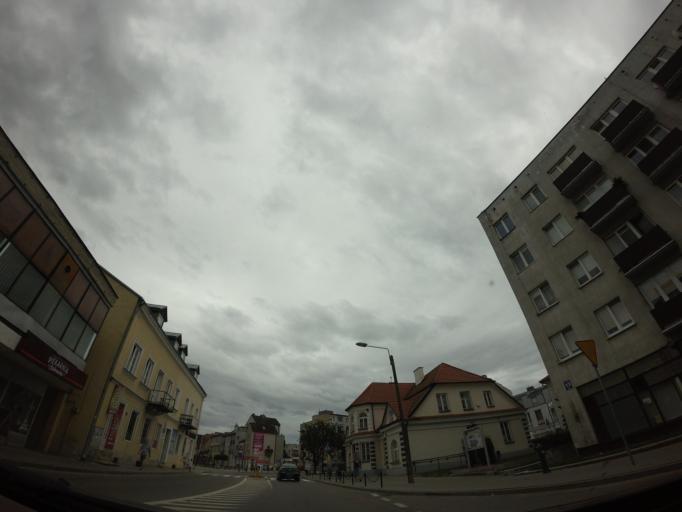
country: PL
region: Masovian Voivodeship
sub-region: Powiat ciechanowski
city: Ciechanow
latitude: 52.8763
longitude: 20.6176
